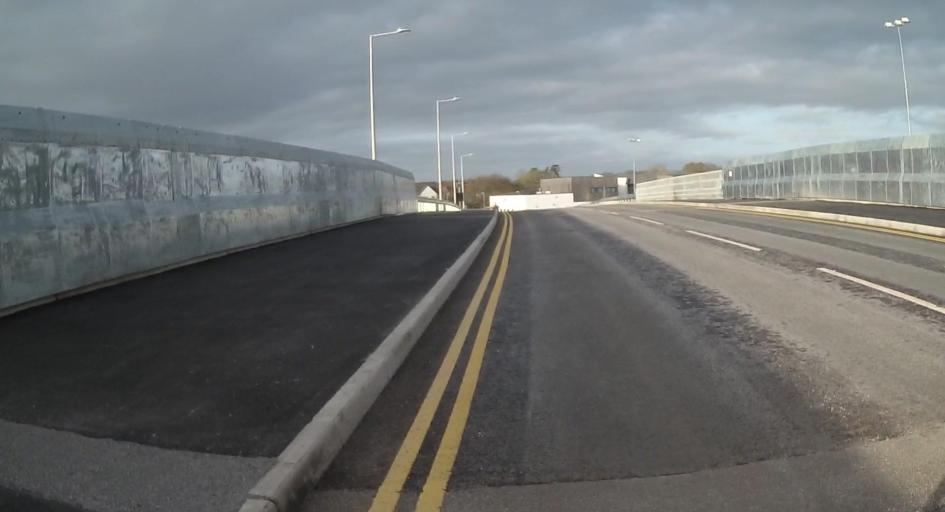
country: GB
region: England
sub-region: Wokingham
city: Wokingham
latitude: 51.4064
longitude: -0.8065
